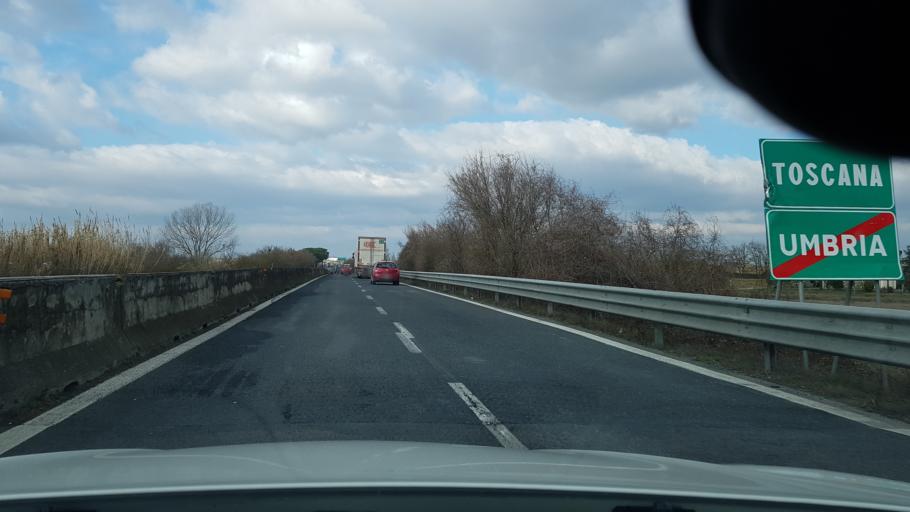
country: IT
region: Tuscany
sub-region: Province of Arezzo
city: Terontola
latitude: 43.1882
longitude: 12.0249
